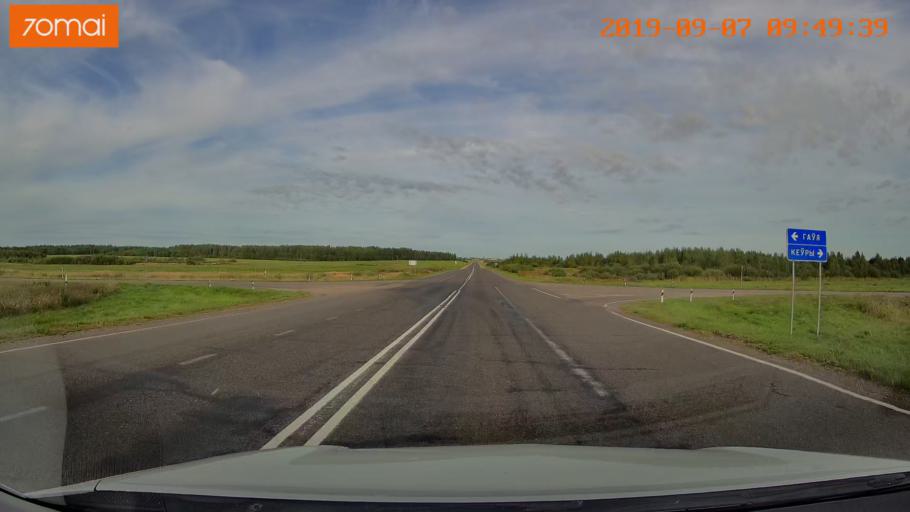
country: BY
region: Grodnenskaya
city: Iwye
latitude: 53.9847
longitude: 25.6593
